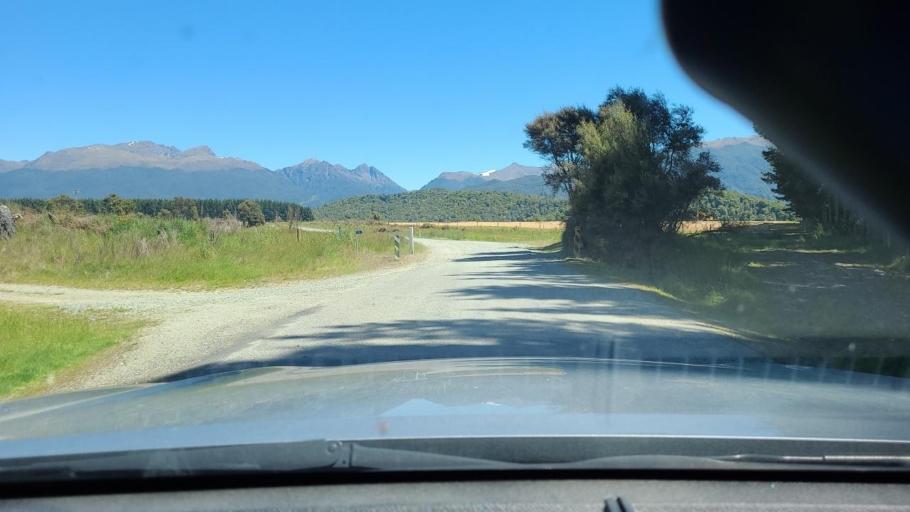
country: NZ
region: Southland
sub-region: Southland District
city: Te Anau
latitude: -45.7782
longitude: 167.5939
